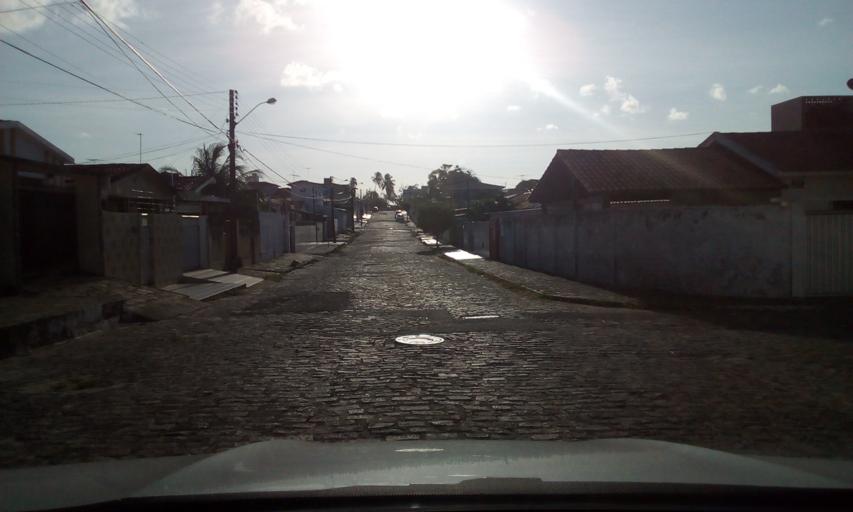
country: BR
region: Paraiba
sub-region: Joao Pessoa
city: Joao Pessoa
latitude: -7.1046
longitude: -34.8560
